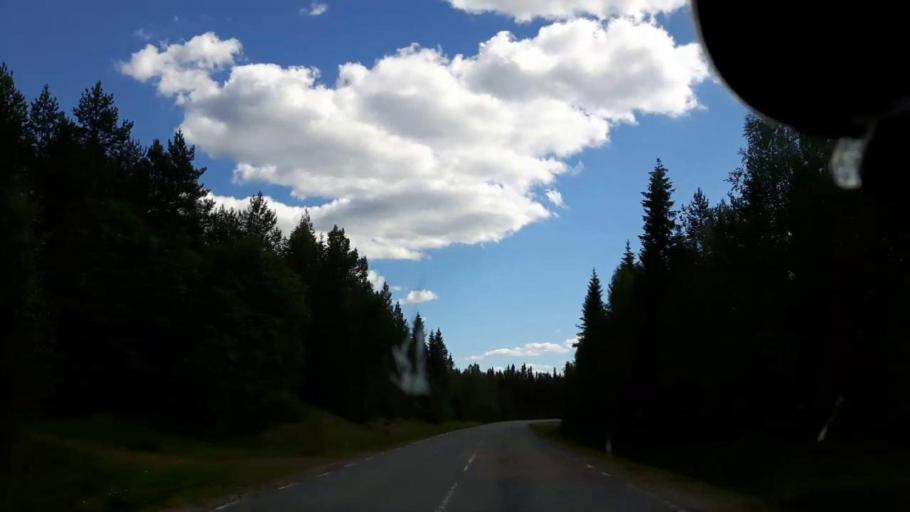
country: SE
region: Vaesternorrland
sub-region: Ange Kommun
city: Fransta
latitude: 62.8253
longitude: 16.1905
